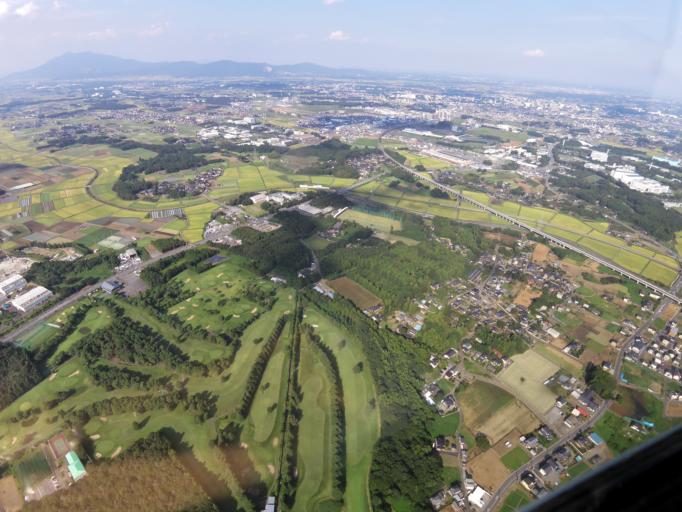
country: JP
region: Ibaraki
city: Mitsukaido
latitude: 36.0702
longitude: 140.0515
